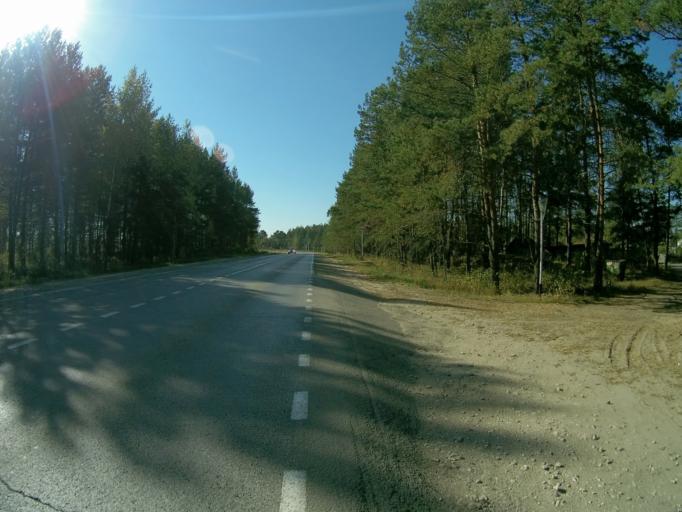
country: RU
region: Vladimir
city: Raduzhnyy
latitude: 56.0254
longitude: 40.3887
